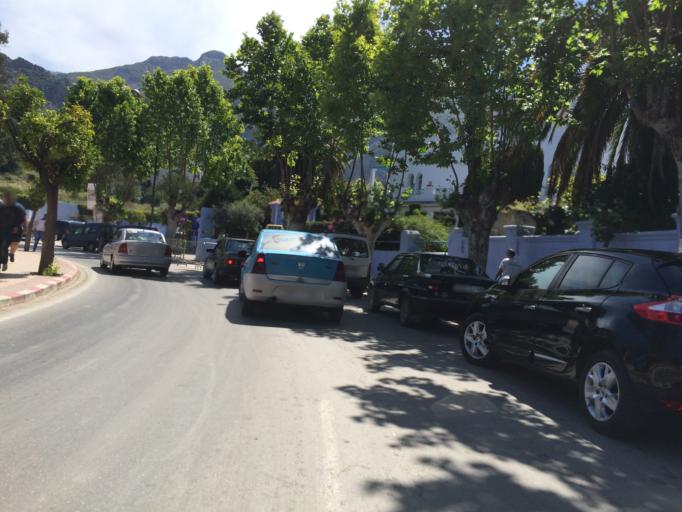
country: MA
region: Tanger-Tetouan
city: Chefchaouene
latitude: 35.1684
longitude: -5.2684
